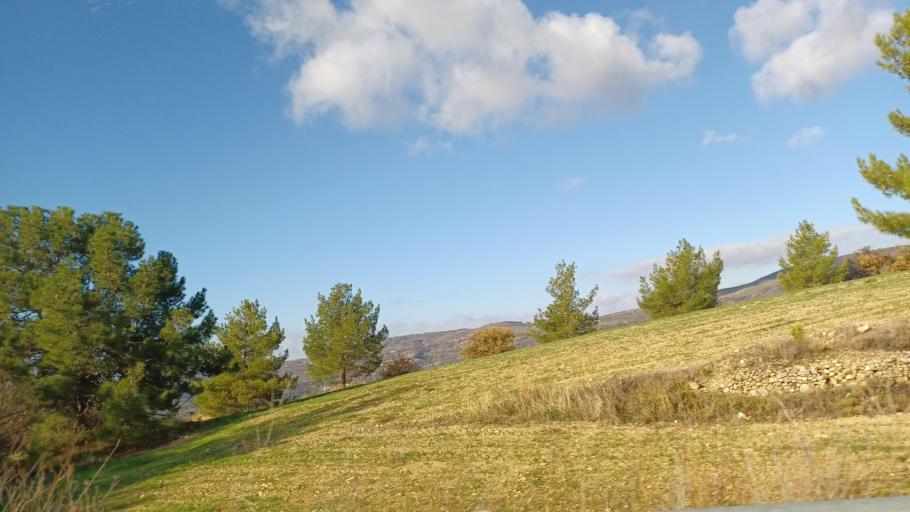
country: CY
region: Limassol
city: Pachna
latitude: 34.8471
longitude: 32.7392
